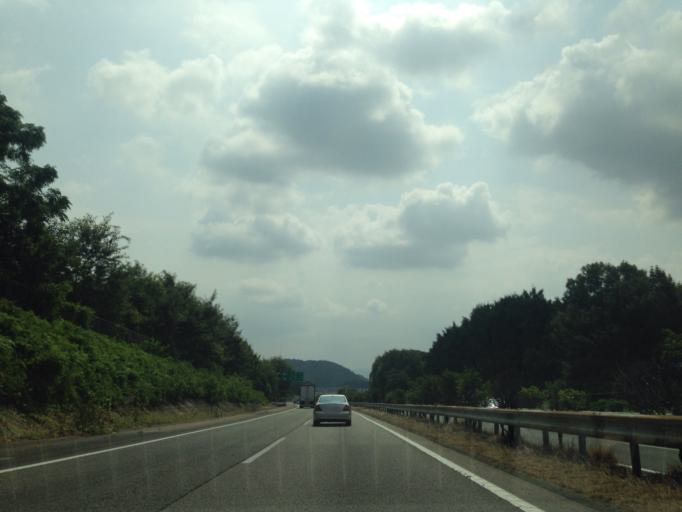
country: JP
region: Aichi
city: Kozakai-cho
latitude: 34.8569
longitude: 137.3318
